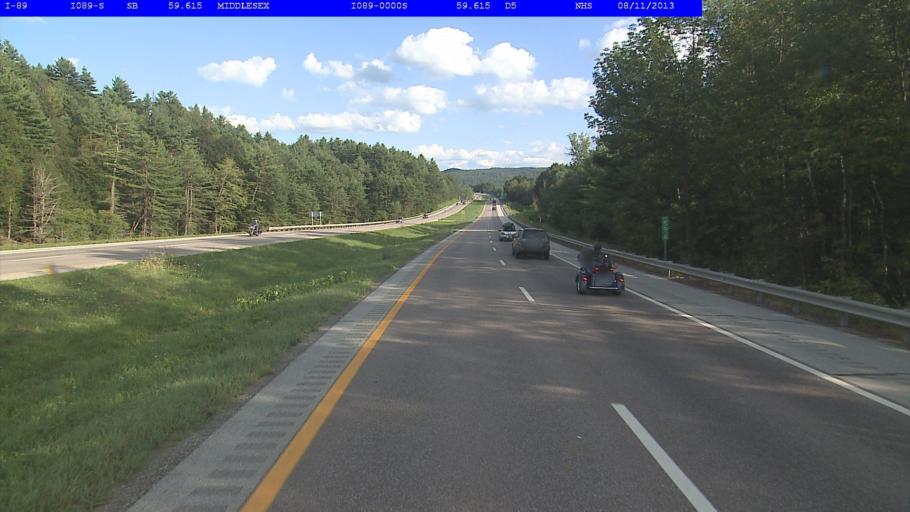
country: US
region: Vermont
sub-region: Washington County
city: Waterbury
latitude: 44.3097
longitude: -72.6932
